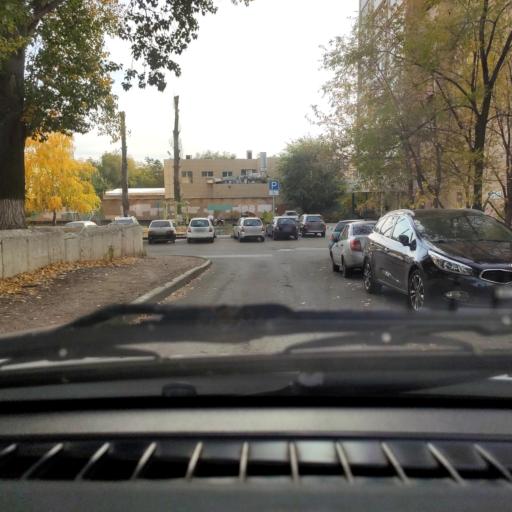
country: RU
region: Samara
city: Zhigulevsk
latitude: 53.4835
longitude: 49.4661
